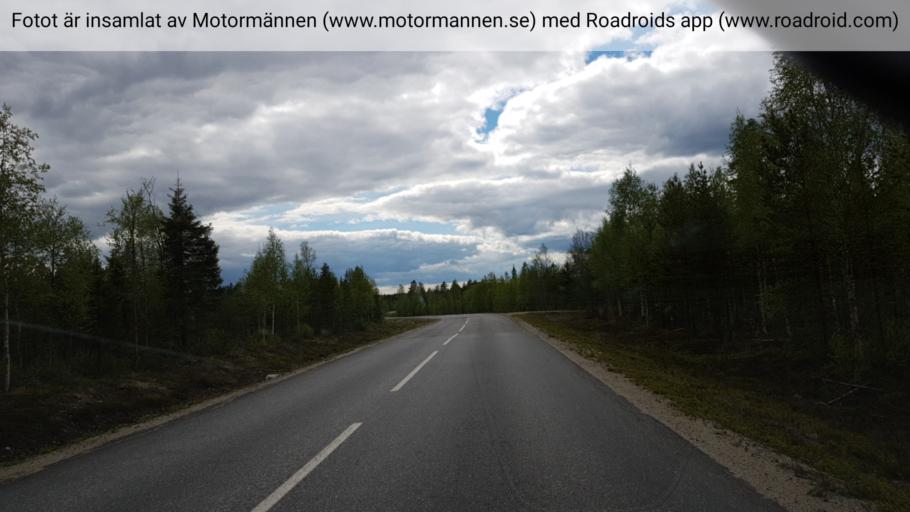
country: SE
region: Vaesterbotten
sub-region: Vindelns Kommun
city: Vindeln
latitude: 64.3859
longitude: 19.6680
